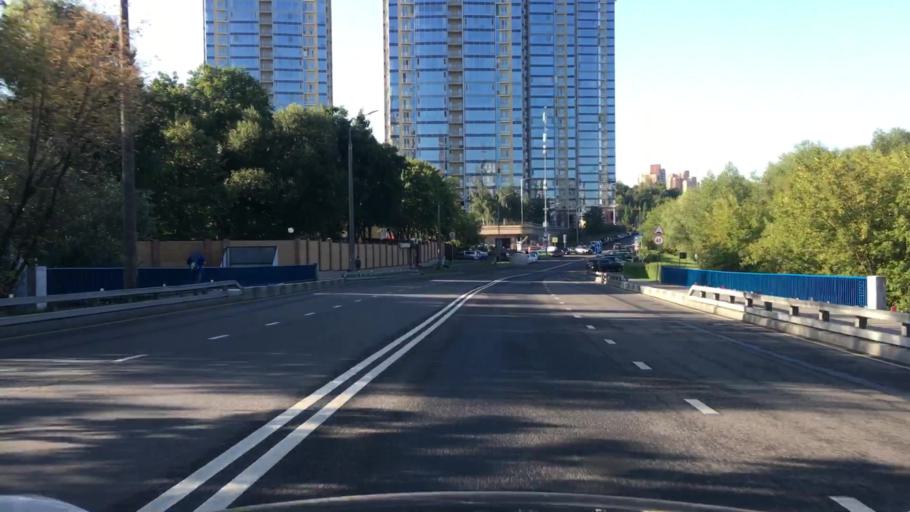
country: RU
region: Moscow
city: Davydkovo
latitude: 55.7215
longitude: 37.4786
